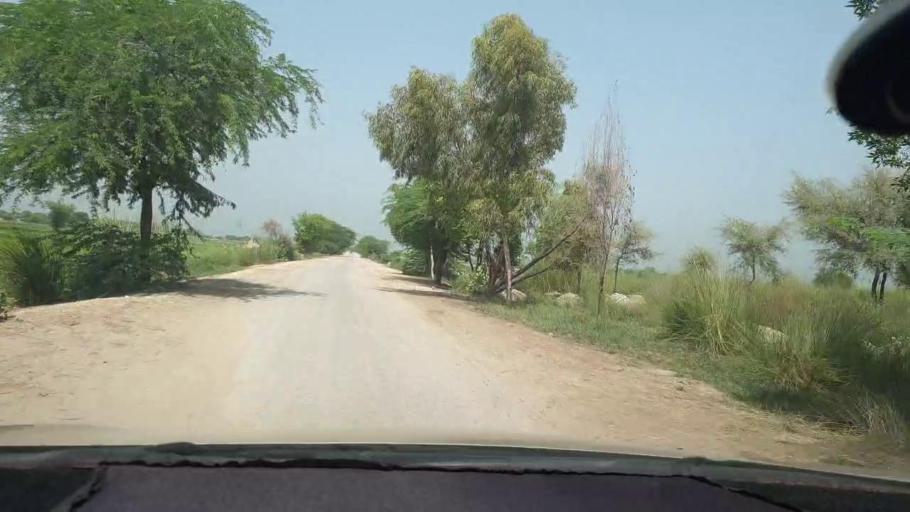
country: PK
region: Sindh
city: Kambar
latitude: 27.6686
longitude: 67.9133
